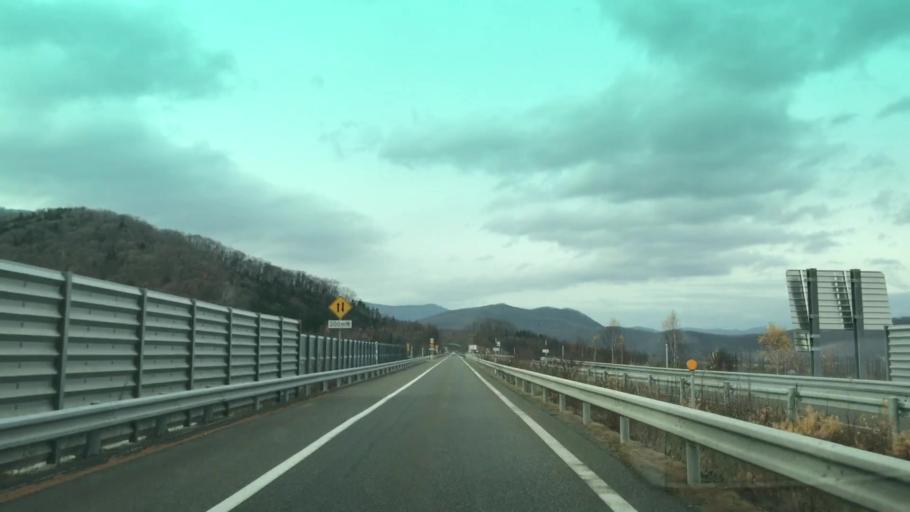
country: JP
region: Hokkaido
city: Otofuke
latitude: 42.9999
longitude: 142.8503
